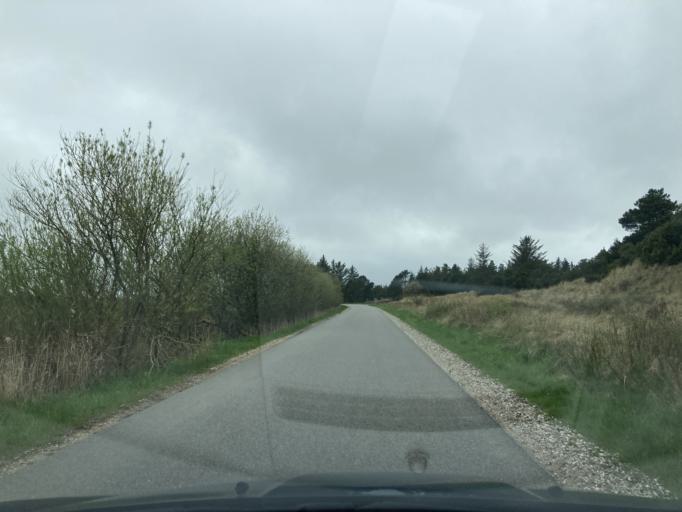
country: DK
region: Central Jutland
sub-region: Lemvig Kommune
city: Thyboron
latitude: 56.8165
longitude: 8.2920
